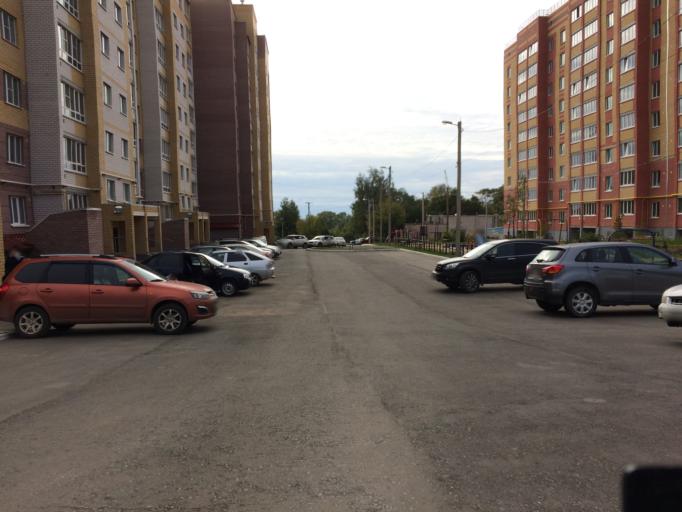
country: RU
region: Mariy-El
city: Yoshkar-Ola
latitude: 56.6510
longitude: 47.9681
